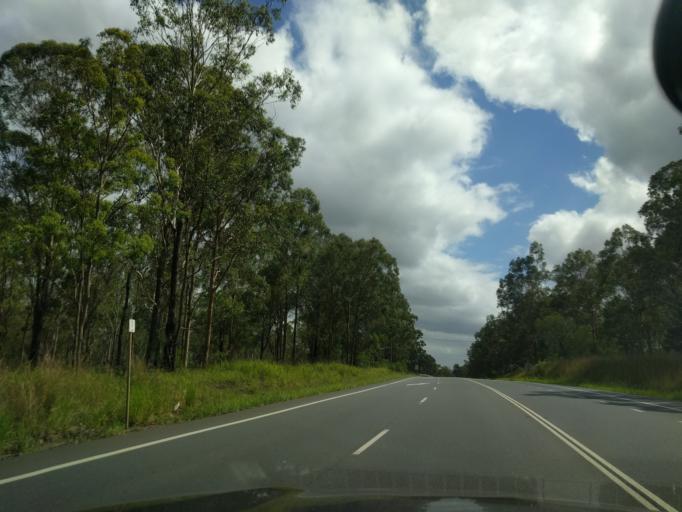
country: AU
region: Queensland
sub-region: Logan
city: Cedar Vale
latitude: -27.8788
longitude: 152.9895
